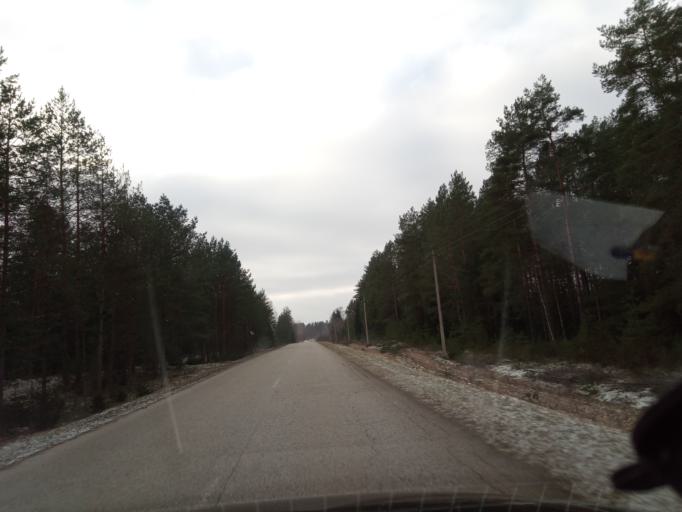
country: LT
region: Alytaus apskritis
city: Varena
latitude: 54.0276
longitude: 24.3543
